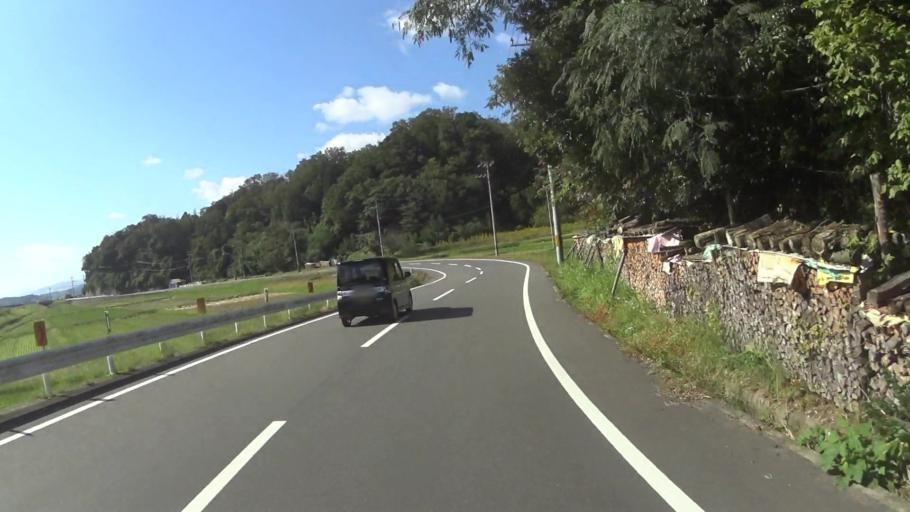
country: JP
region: Kyoto
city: Miyazu
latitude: 35.6929
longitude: 135.0975
